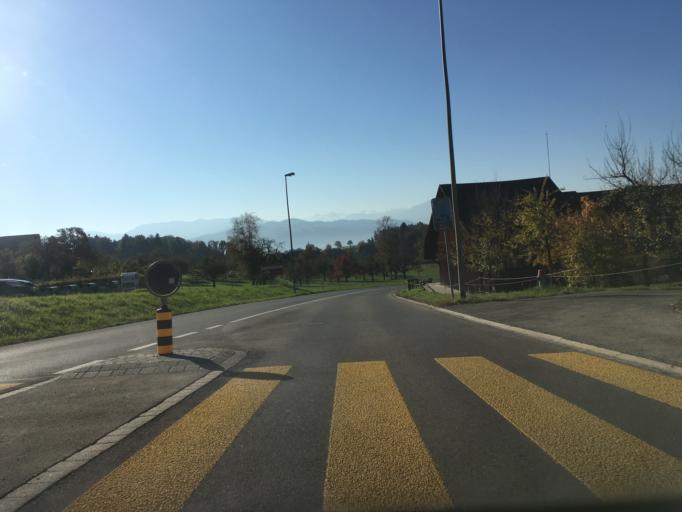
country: CH
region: Zurich
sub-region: Bezirk Affoltern
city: Hausen am Albis / Hausen (Dorf)
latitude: 47.2273
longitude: 8.5268
